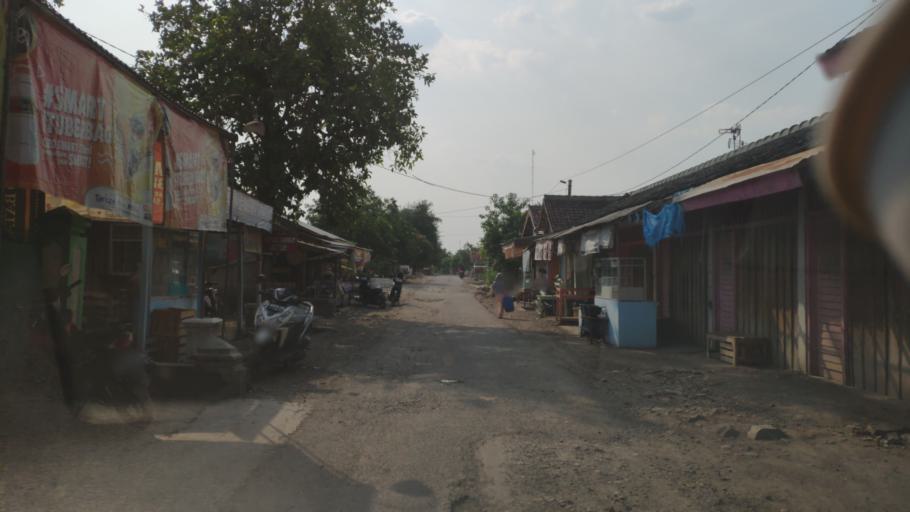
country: ID
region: Central Java
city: Randublatung
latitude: -7.2810
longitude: 111.2494
